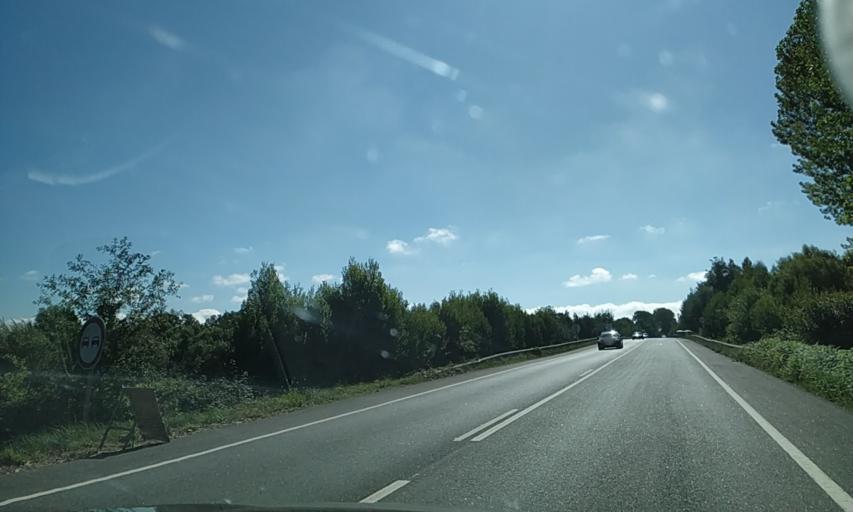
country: PT
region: Aveiro
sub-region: Aveiro
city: Eixo
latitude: 40.6822
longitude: -8.5772
